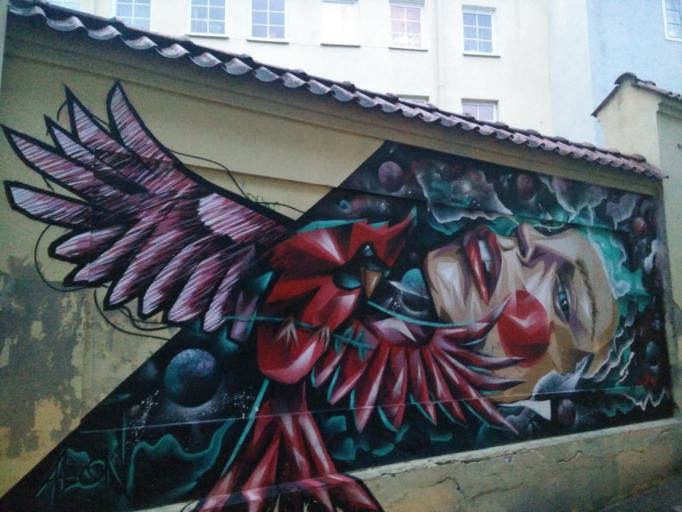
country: LT
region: Vilnius County
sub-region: Vilnius
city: Vilnius
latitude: 54.6822
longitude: 25.2900
